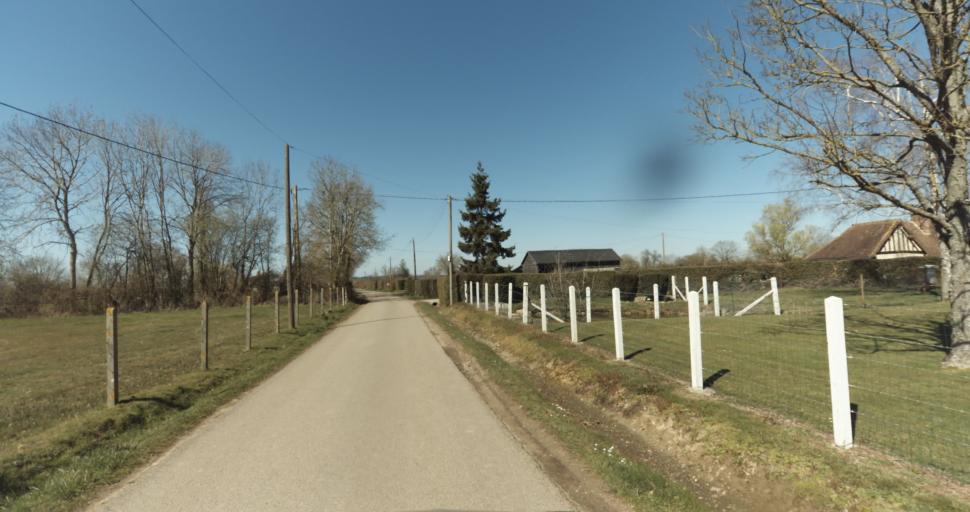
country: FR
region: Lower Normandy
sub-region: Departement du Calvados
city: Livarot
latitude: 48.9958
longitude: 0.1071
